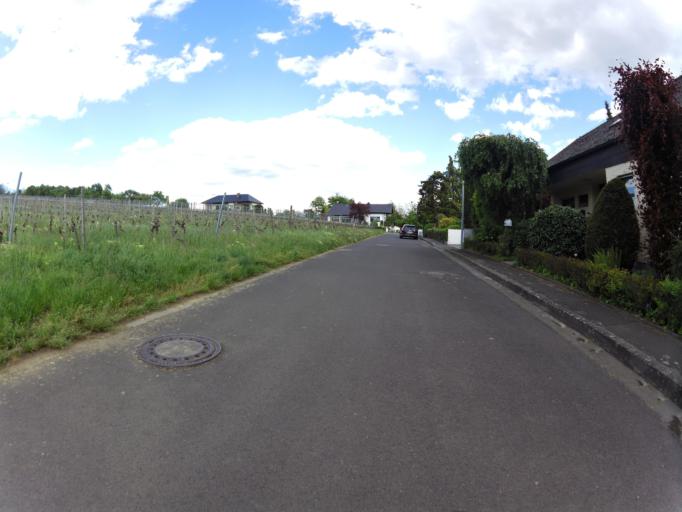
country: DE
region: Bavaria
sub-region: Regierungsbezirk Unterfranken
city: Volkach
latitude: 49.8723
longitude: 10.2234
